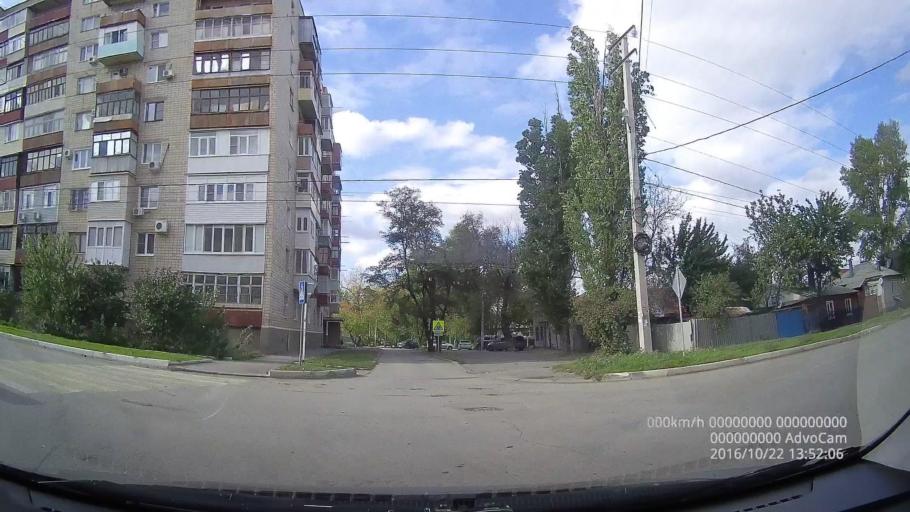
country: RU
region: Rostov
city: Kamensk-Shakhtinskiy
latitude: 48.3149
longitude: 40.2605
